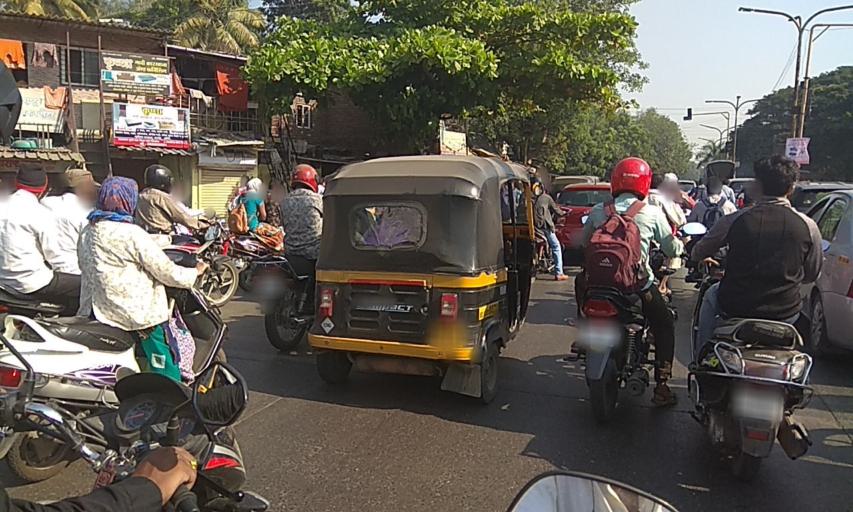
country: IN
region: Maharashtra
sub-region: Pune Division
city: Pune
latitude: 18.4959
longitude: 73.8381
